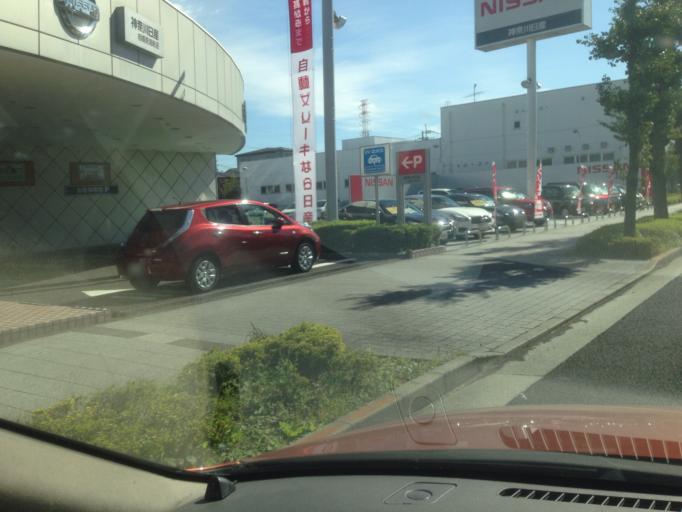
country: JP
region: Tokyo
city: Hachioji
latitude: 35.5807
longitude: 139.3586
